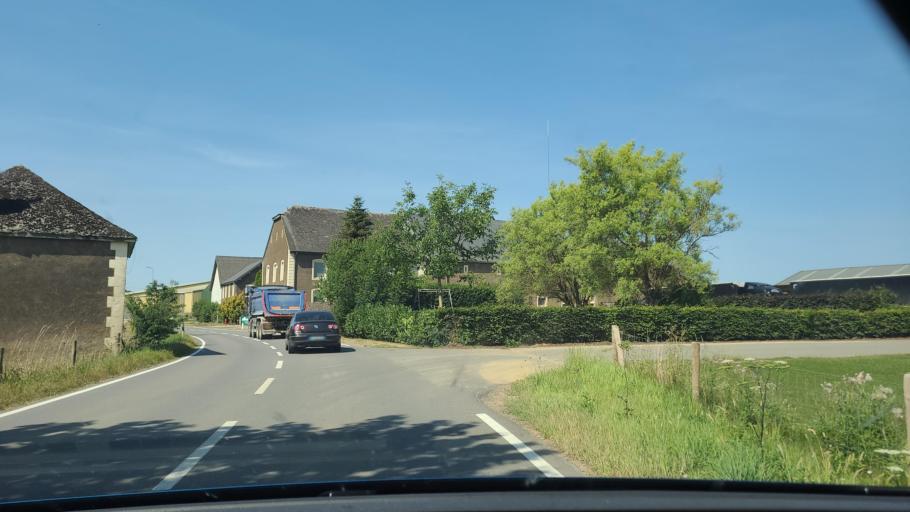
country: LU
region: Luxembourg
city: Soleuvre
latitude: 49.5435
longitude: 5.9587
